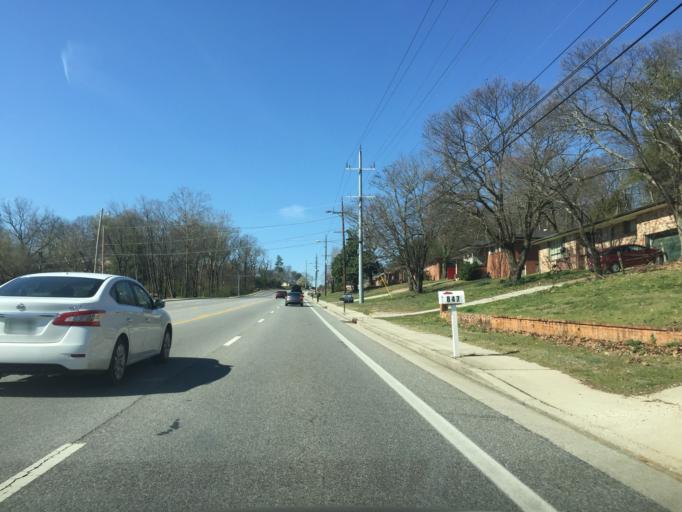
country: US
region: Tennessee
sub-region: Hamilton County
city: Red Bank
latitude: 35.1171
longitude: -85.2694
